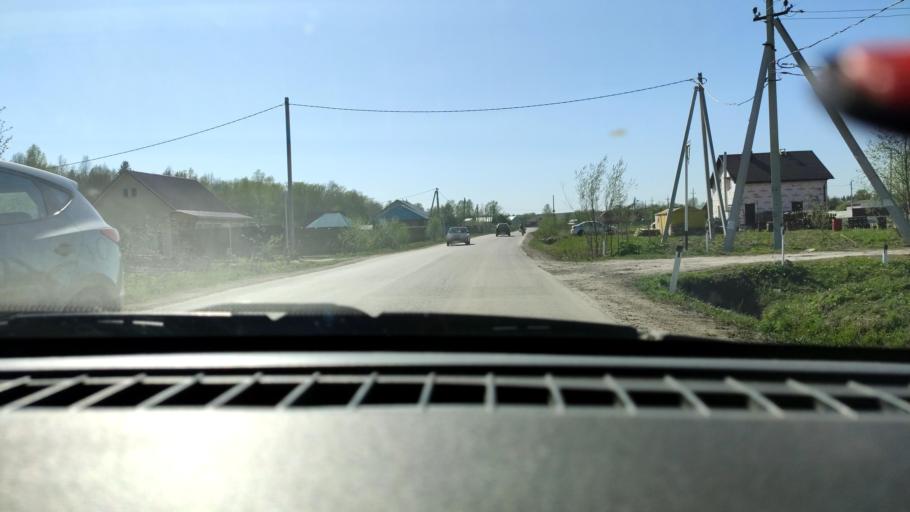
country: RU
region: Perm
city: Overyata
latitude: 58.0788
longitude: 55.9955
